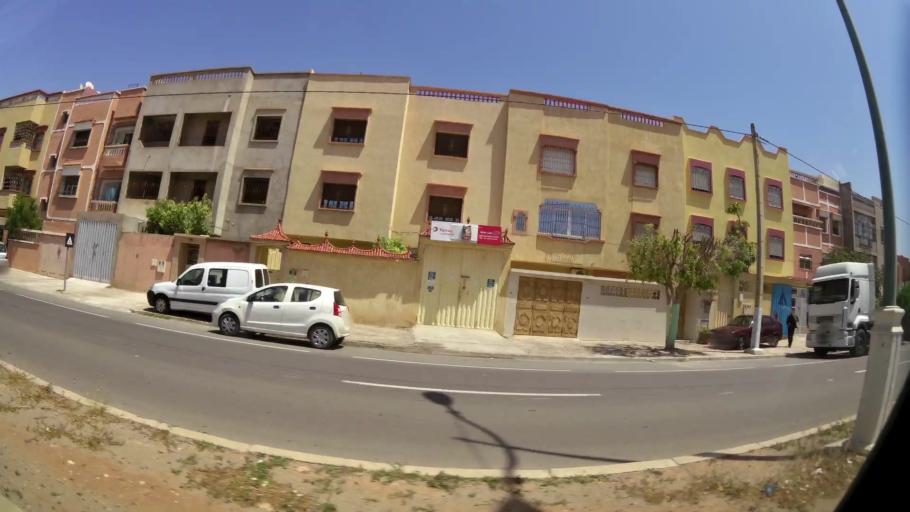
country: MA
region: Souss-Massa-Draa
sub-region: Inezgane-Ait Mellou
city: Inezgane
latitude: 30.3468
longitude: -9.4847
